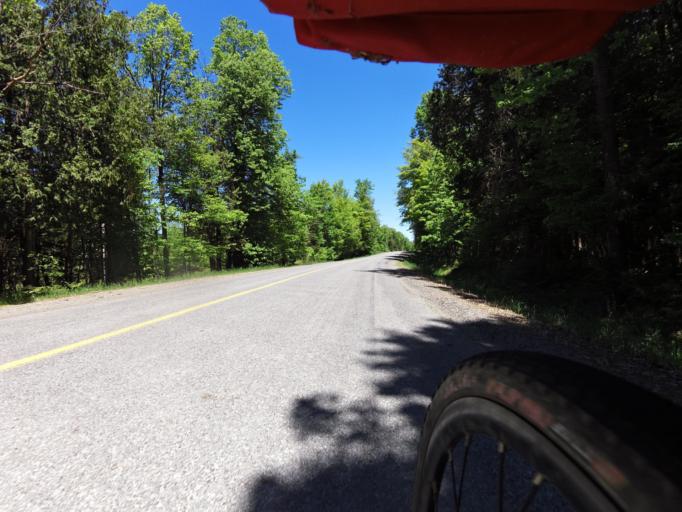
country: CA
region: Ontario
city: Carleton Place
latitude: 45.1721
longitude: -76.4126
